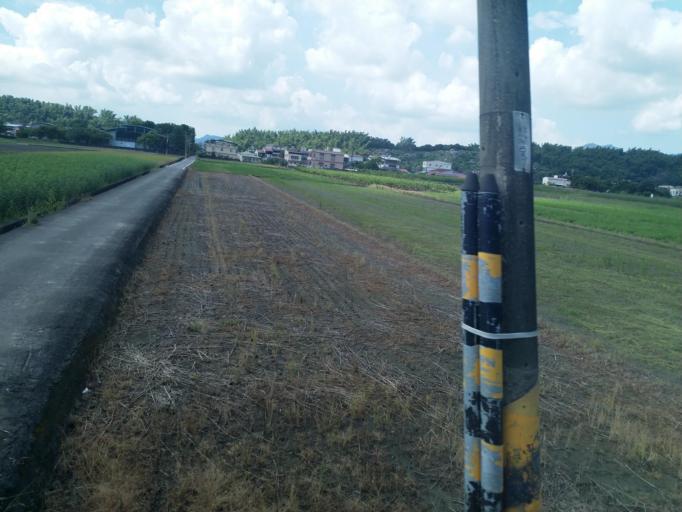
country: TW
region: Taiwan
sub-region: Pingtung
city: Pingtung
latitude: 22.8786
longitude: 120.5751
